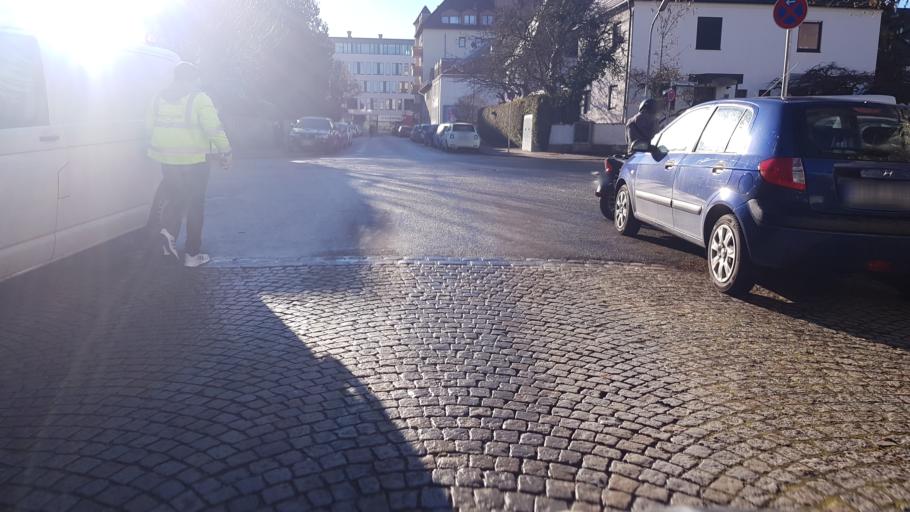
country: DE
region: Bavaria
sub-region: Upper Bavaria
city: Munich
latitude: 48.1181
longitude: 11.5315
